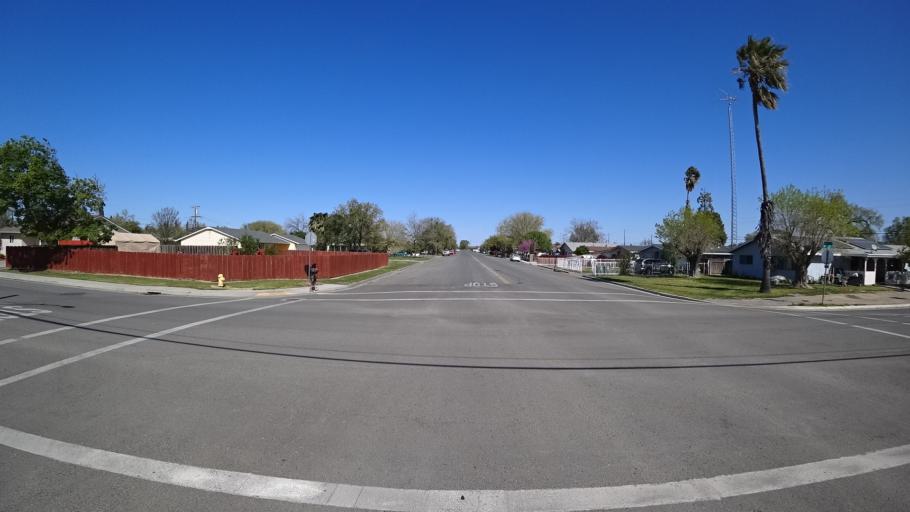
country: US
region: California
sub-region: Glenn County
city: Hamilton City
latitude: 39.7430
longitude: -122.0127
